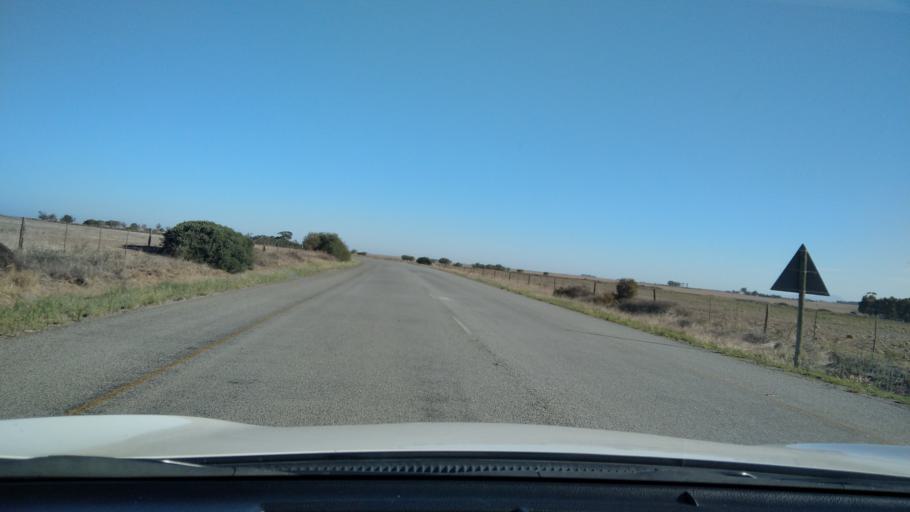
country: ZA
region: Western Cape
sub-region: West Coast District Municipality
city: Moorreesburg
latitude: -33.2600
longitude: 18.5924
